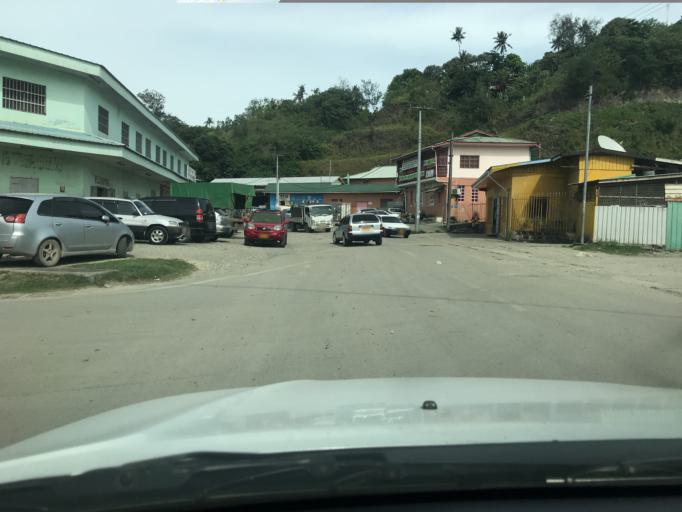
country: SB
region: Guadalcanal
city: Honiara
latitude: -9.4391
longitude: 159.9642
